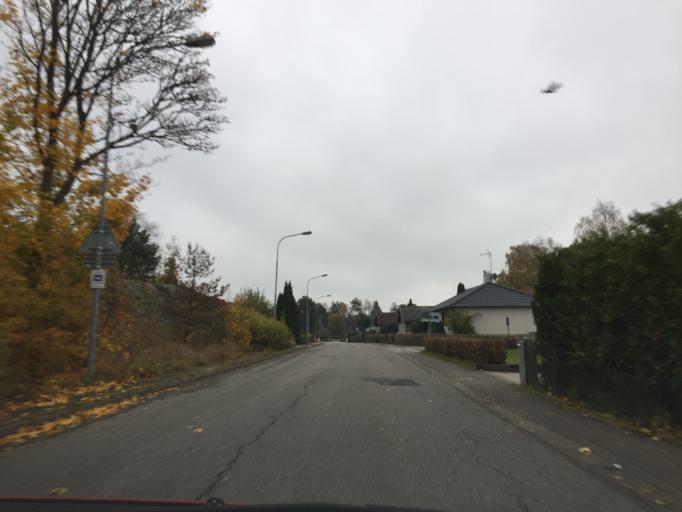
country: SE
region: Vaestra Goetaland
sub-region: Trollhattan
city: Trollhattan
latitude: 58.2654
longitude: 12.2880
